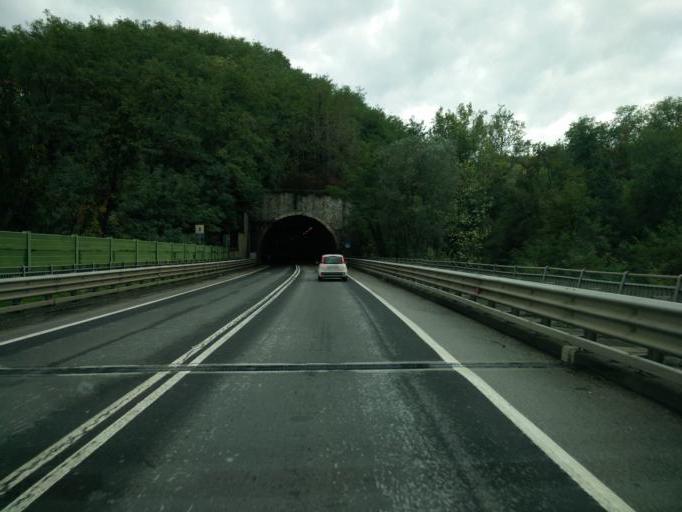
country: IT
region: Tuscany
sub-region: Provincia di Lucca
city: Valdottavo
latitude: 43.9119
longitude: 10.5242
